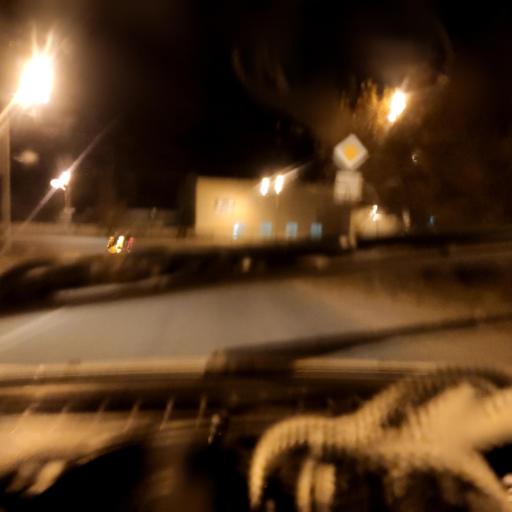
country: RU
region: Samara
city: Zhigulevsk
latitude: 53.4650
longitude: 49.5485
